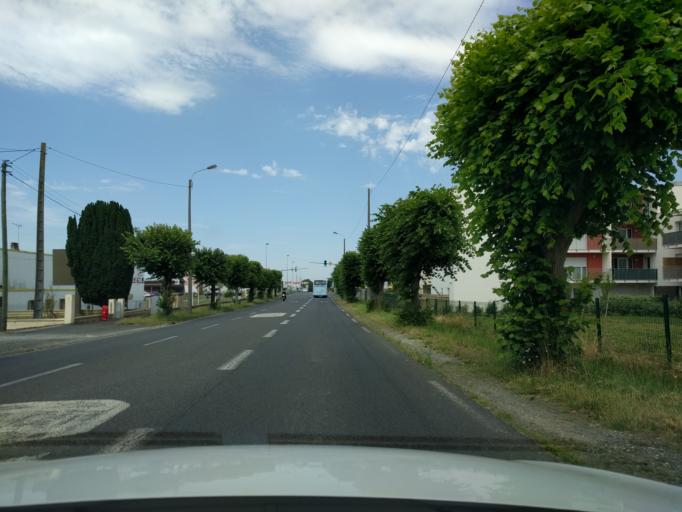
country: FR
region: Poitou-Charentes
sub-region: Departement des Deux-Sevres
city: Niort
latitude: 46.3405
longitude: -0.4877
